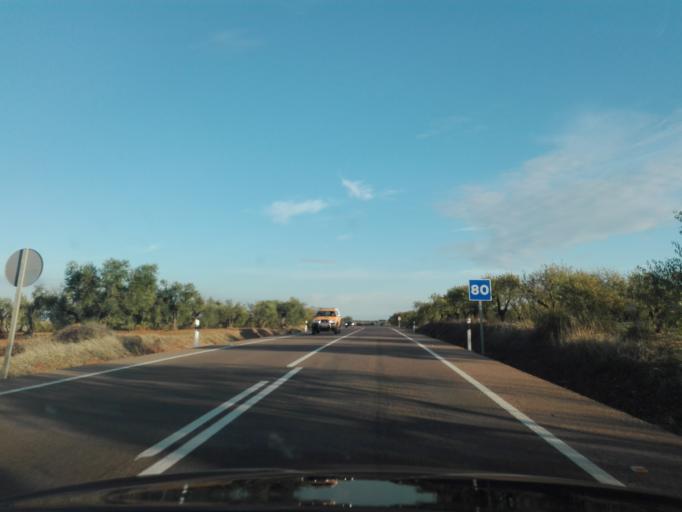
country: ES
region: Extremadura
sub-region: Provincia de Badajoz
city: Usagre
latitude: 38.3456
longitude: -6.1839
